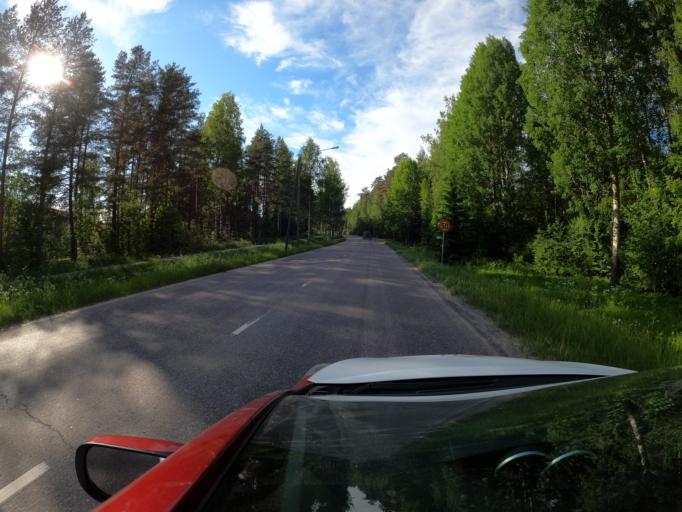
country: FI
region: Southern Savonia
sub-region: Savonlinna
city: Savonlinna
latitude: 61.8503
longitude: 28.9643
